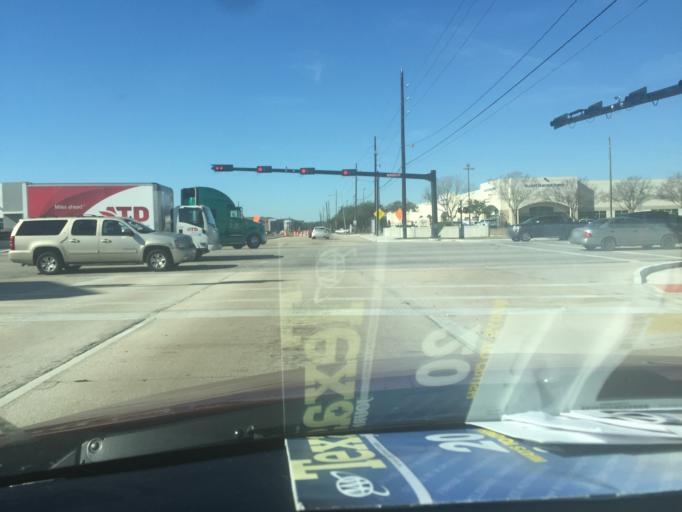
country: US
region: Texas
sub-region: Fort Bend County
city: Meadows Place
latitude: 29.6413
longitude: -95.5649
